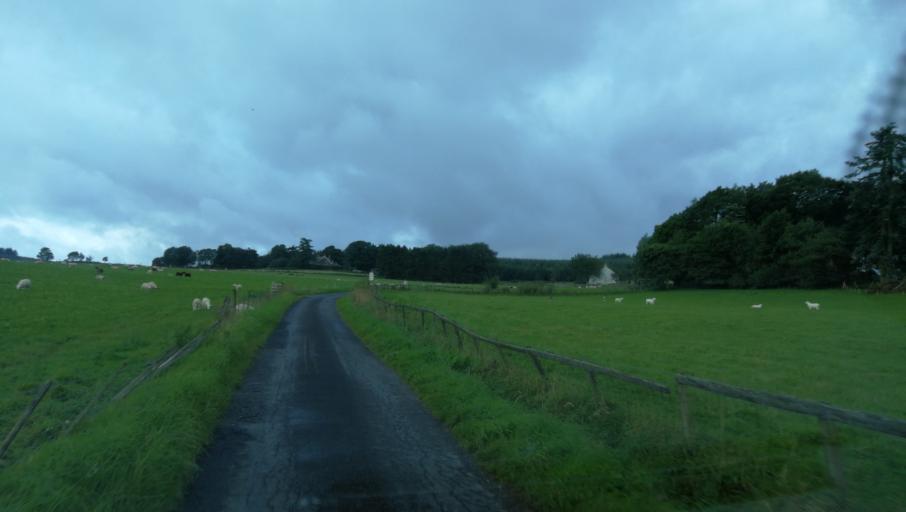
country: GB
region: Scotland
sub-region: Perth and Kinross
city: Alyth
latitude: 56.6260
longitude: -3.2736
